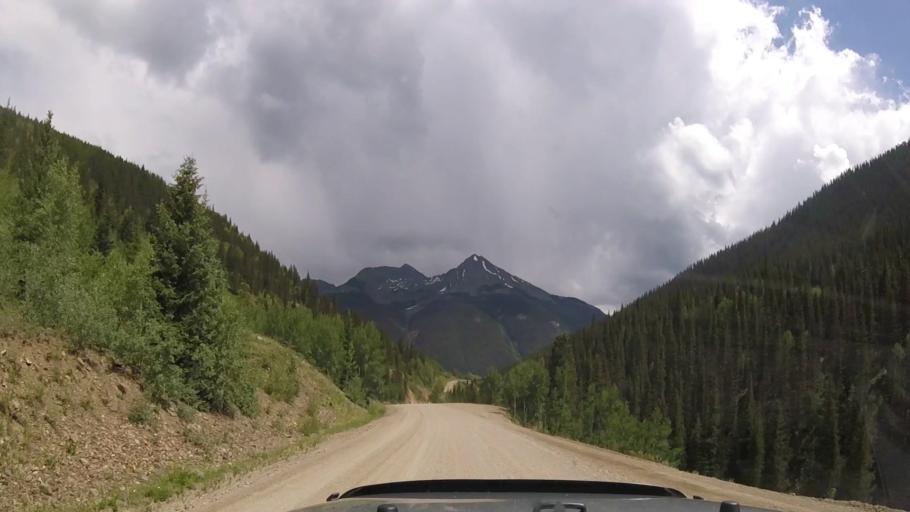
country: US
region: Colorado
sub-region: San Juan County
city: Silverton
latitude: 37.8271
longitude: -107.6689
